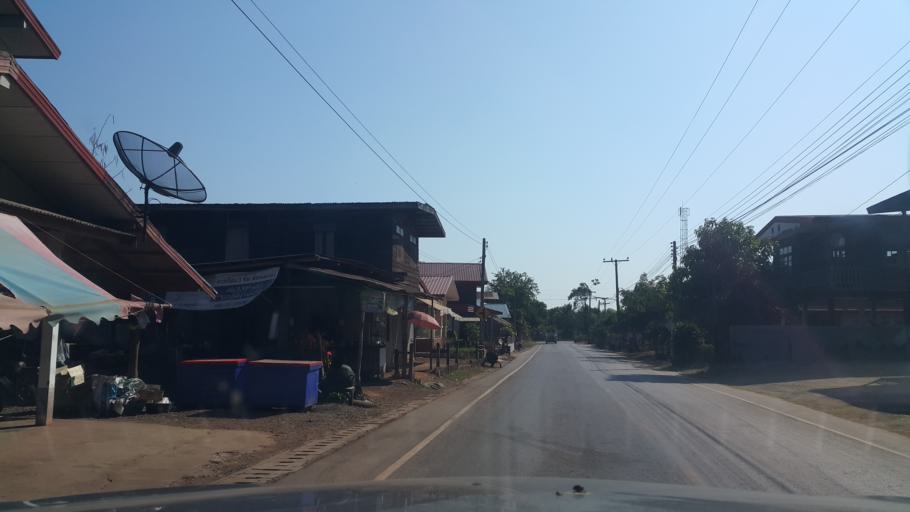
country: TH
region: Changwat Udon Thani
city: Ban Dung
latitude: 17.7155
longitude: 103.3910
